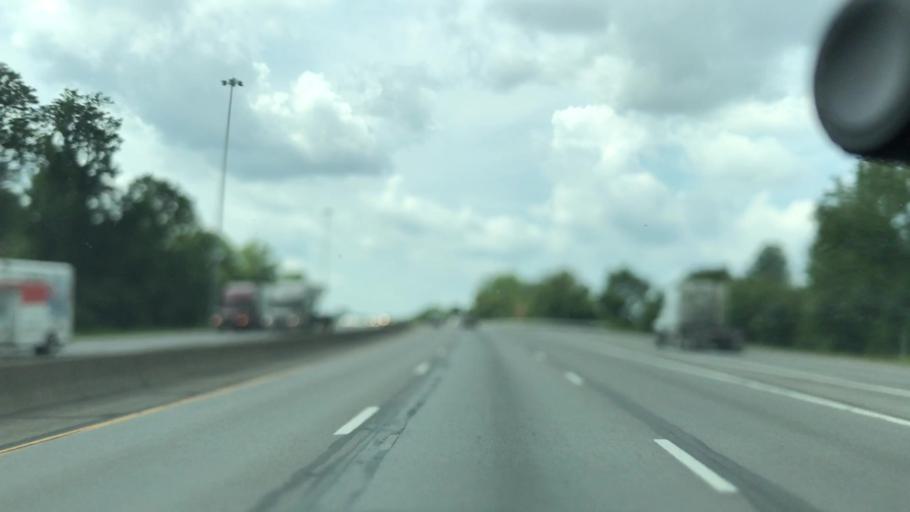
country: US
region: West Virginia
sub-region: Kanawha County
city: South Charleston
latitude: 38.3644
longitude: -81.6885
